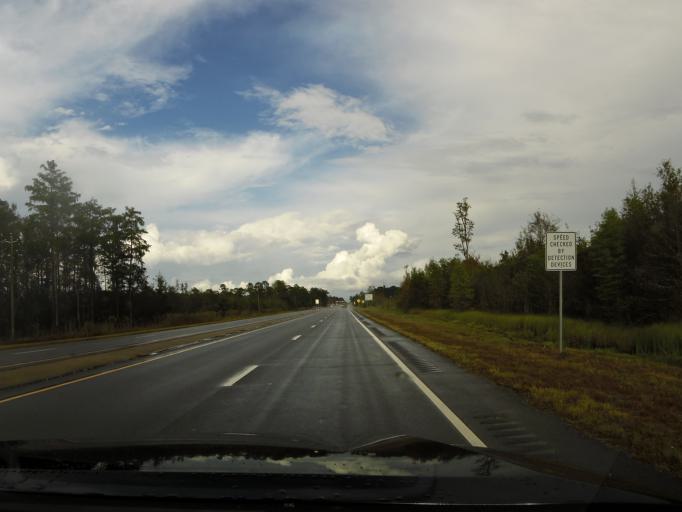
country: US
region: Georgia
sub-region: Liberty County
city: Walthourville
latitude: 31.7697
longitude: -81.6401
